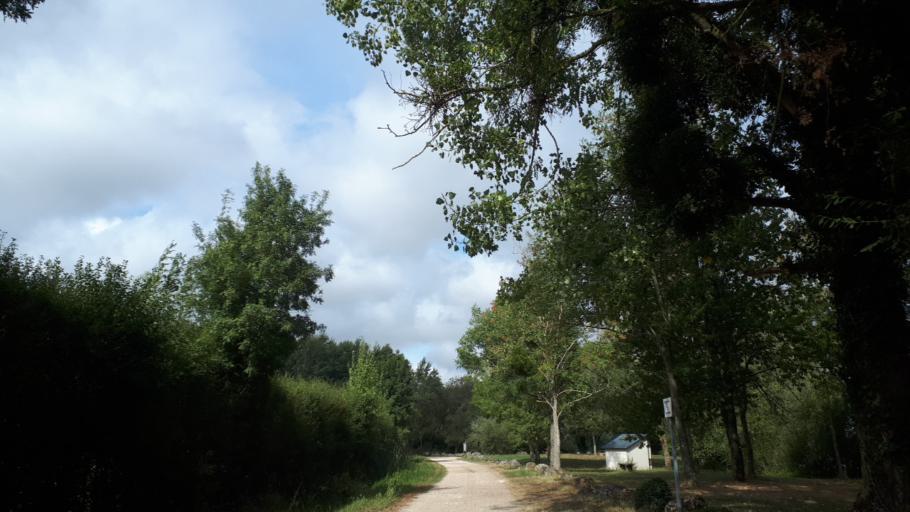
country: FR
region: Centre
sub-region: Departement du Loir-et-Cher
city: Villiers-sur-Loir
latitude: 47.7871
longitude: 0.9969
